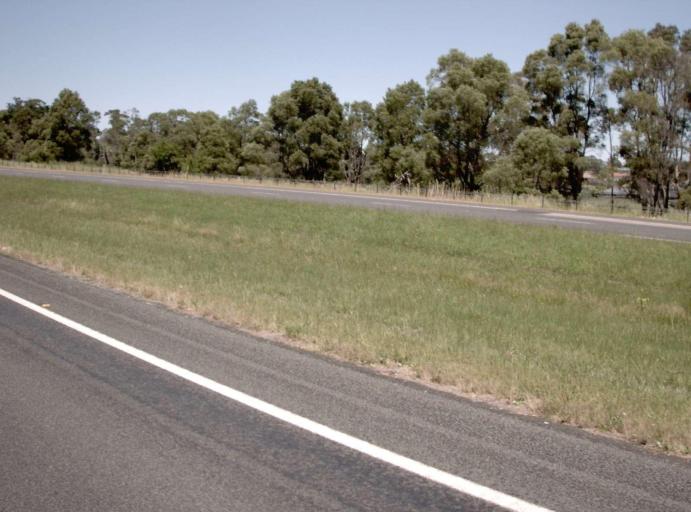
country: AU
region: Victoria
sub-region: Baw Baw
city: Warragul
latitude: -38.1280
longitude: 145.8746
